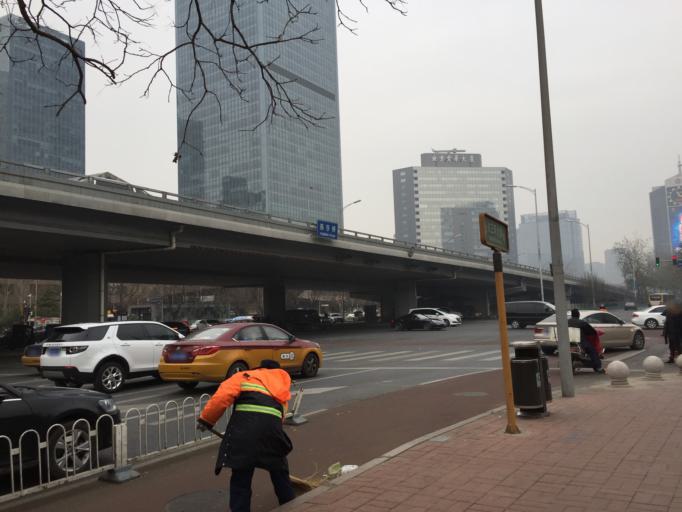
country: CN
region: Beijing
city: Chaowai
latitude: 39.9476
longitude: 116.4559
